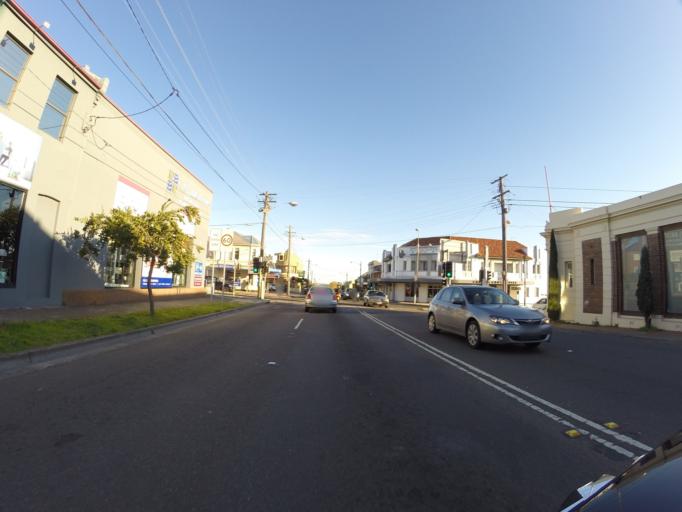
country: AU
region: New South Wales
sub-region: Waverley
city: Bondi Junction
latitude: -33.8998
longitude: 151.2537
